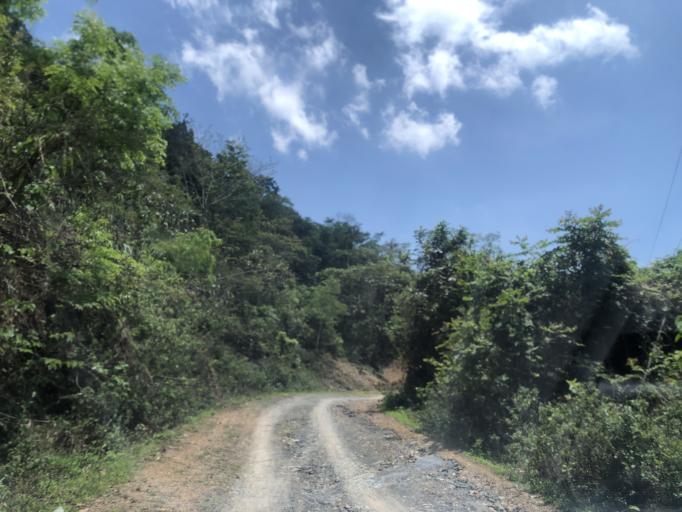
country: LA
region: Phongsali
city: Phongsali
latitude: 21.4454
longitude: 102.1637
